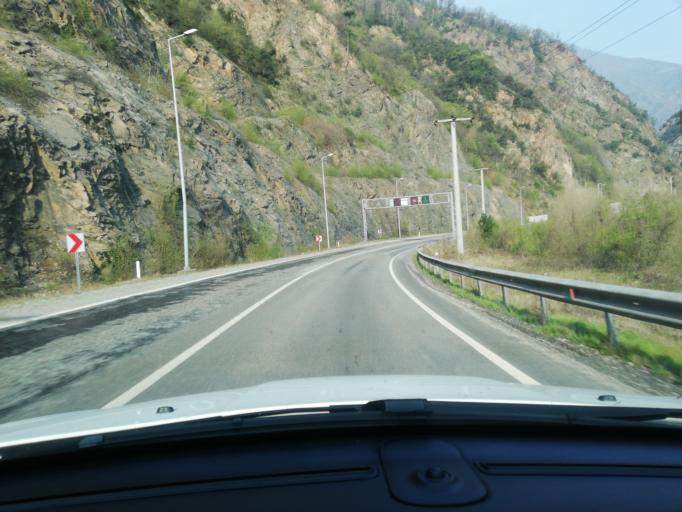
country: TR
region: Karabuk
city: Yenice
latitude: 41.1587
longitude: 32.4612
